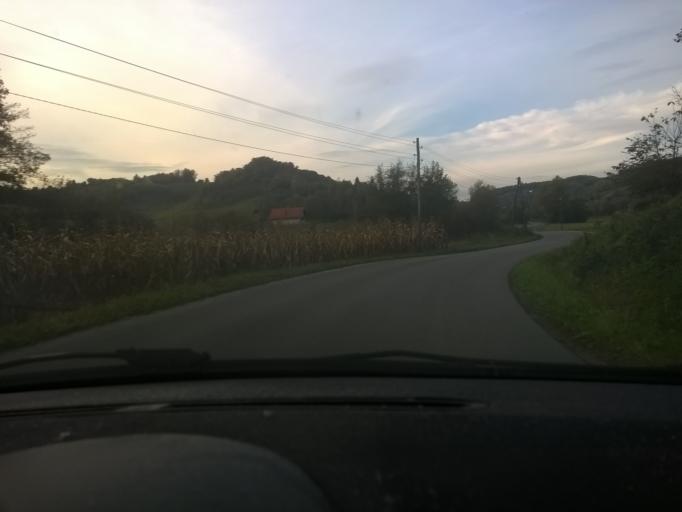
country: HR
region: Krapinsko-Zagorska
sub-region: Grad Krapina
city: Krapina
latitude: 46.1147
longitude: 15.8630
